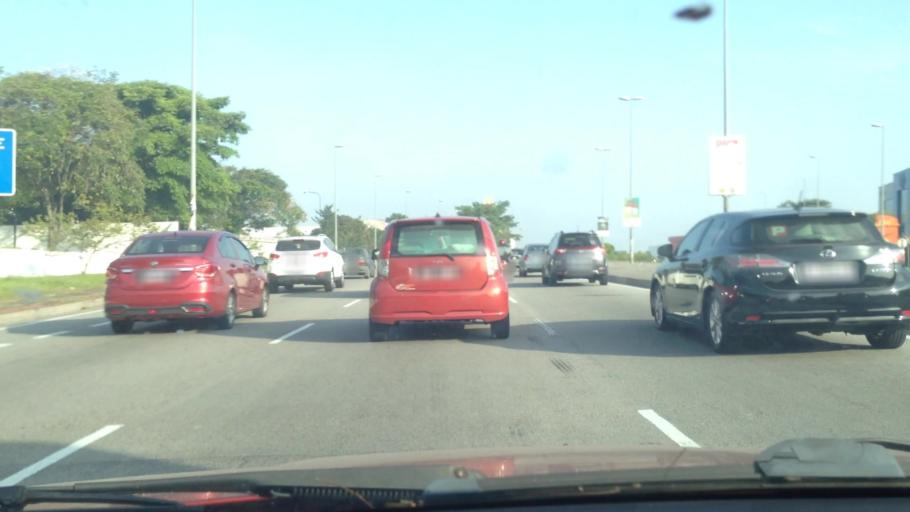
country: MY
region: Selangor
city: Subang Jaya
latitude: 3.0432
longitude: 101.5464
